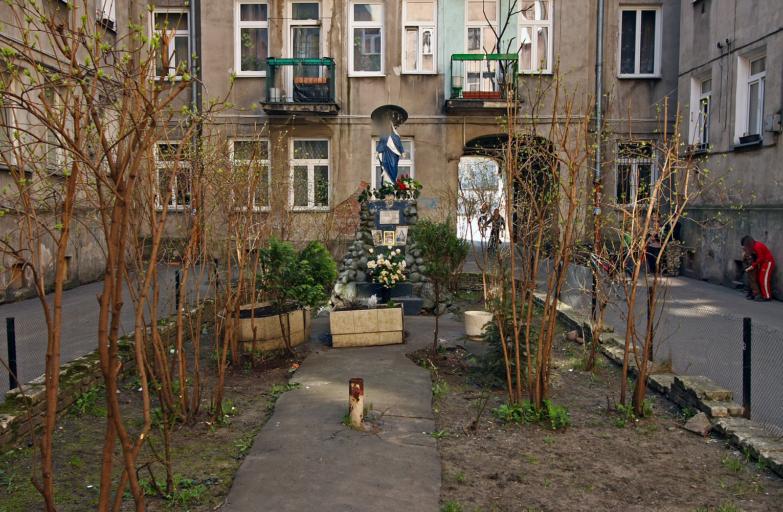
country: PL
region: Masovian Voivodeship
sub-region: Warszawa
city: Praga Polnoc
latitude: 52.2520
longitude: 21.0421
